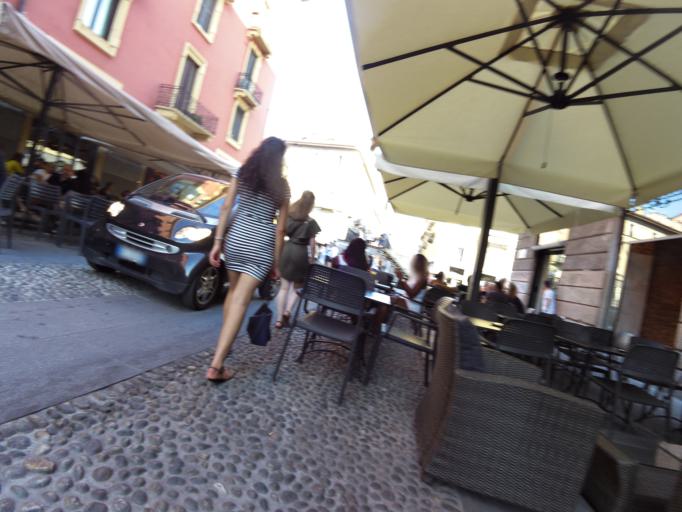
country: IT
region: Lombardy
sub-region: Citta metropolitana di Milano
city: Milano
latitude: 45.4514
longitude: 9.1709
